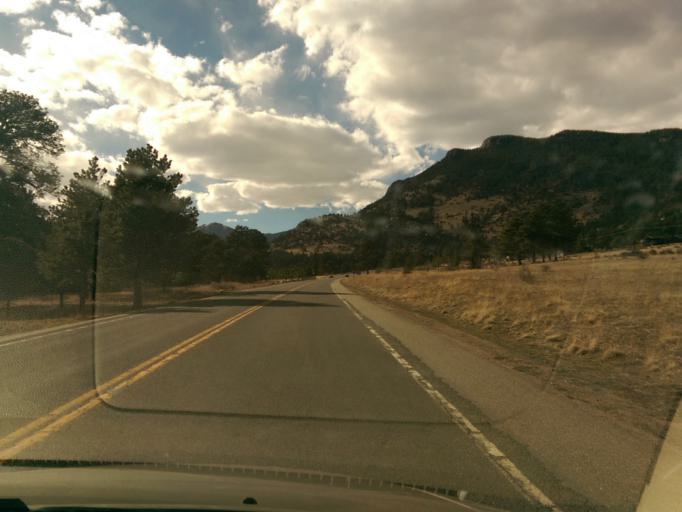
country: US
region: Colorado
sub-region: Larimer County
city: Estes Park
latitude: 40.3660
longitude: -105.5575
